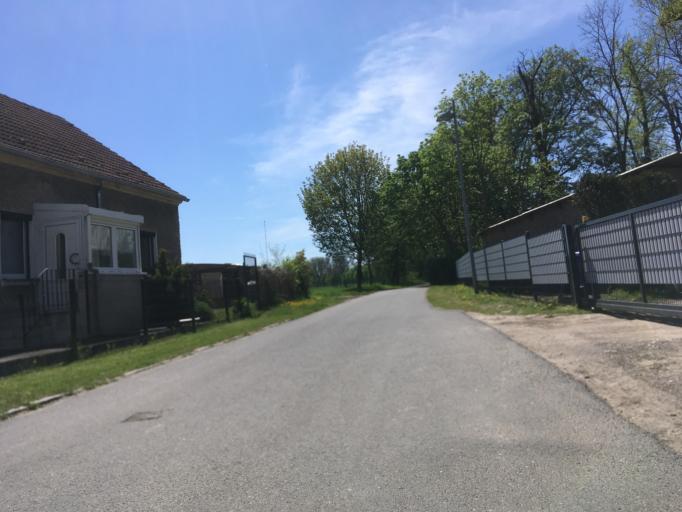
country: DE
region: Brandenburg
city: Wildau
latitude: 52.3202
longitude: 13.6138
